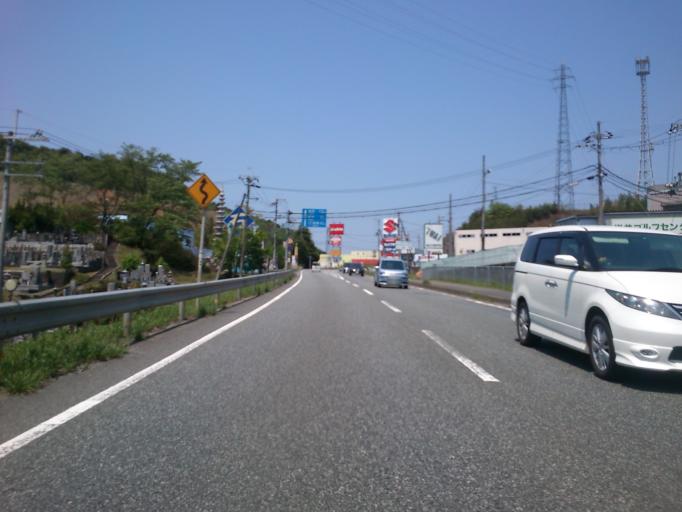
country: JP
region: Kyoto
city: Fukuchiyama
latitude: 35.3135
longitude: 135.1019
